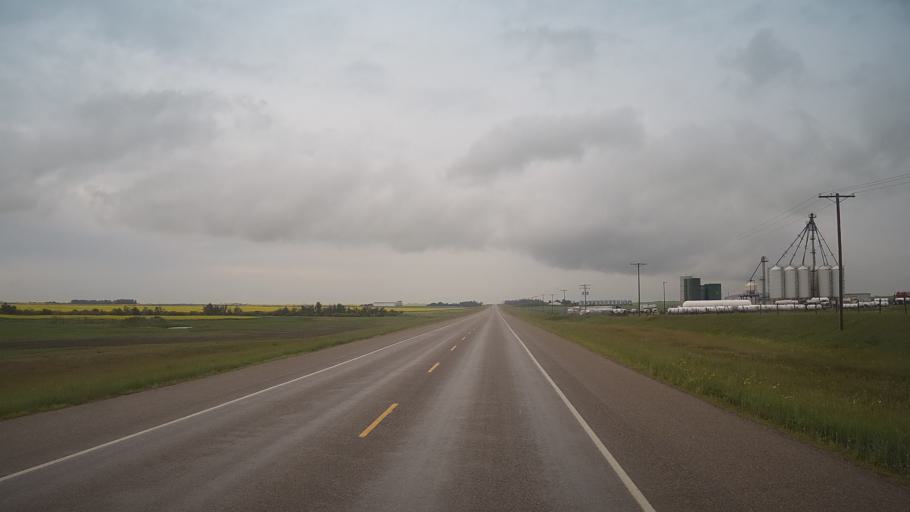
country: CA
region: Saskatchewan
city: Wilkie
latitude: 52.4057
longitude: -108.7539
